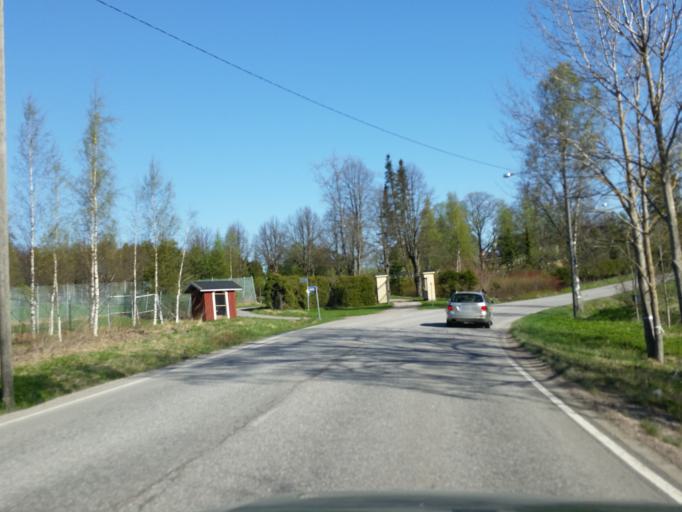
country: FI
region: Uusimaa
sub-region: Helsinki
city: Kirkkonummi
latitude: 60.1823
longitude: 24.3919
